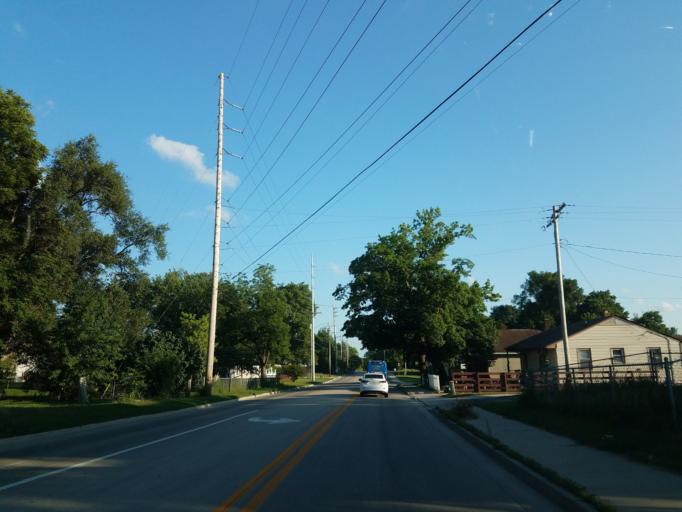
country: US
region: Illinois
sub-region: McLean County
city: Bloomington
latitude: 40.4760
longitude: -89.0162
